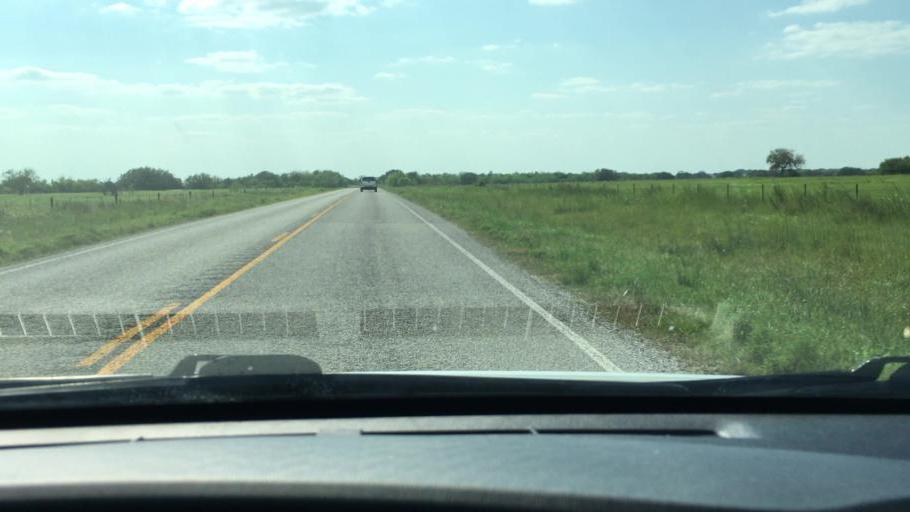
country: US
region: Texas
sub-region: DeWitt County
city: Yorktown
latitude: 28.9188
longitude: -97.3370
